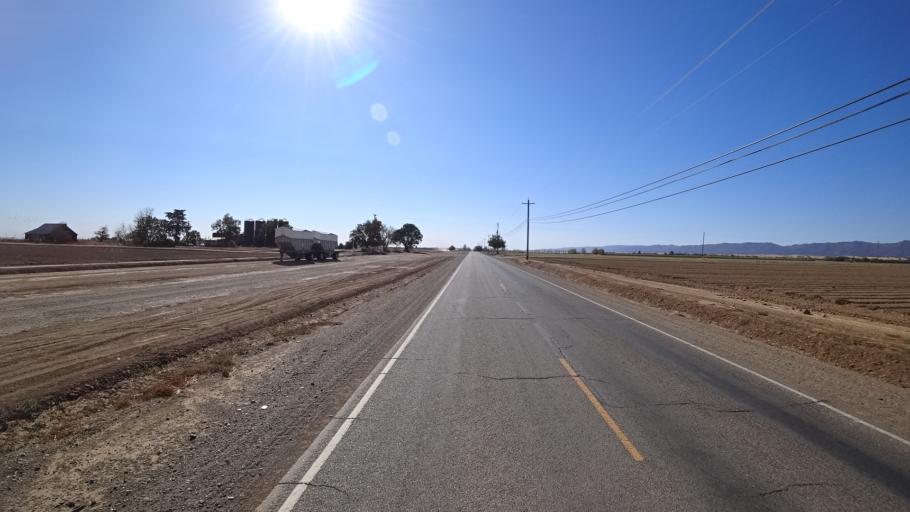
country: US
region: California
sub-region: Yolo County
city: Cottonwood
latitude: 38.6483
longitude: -121.9712
